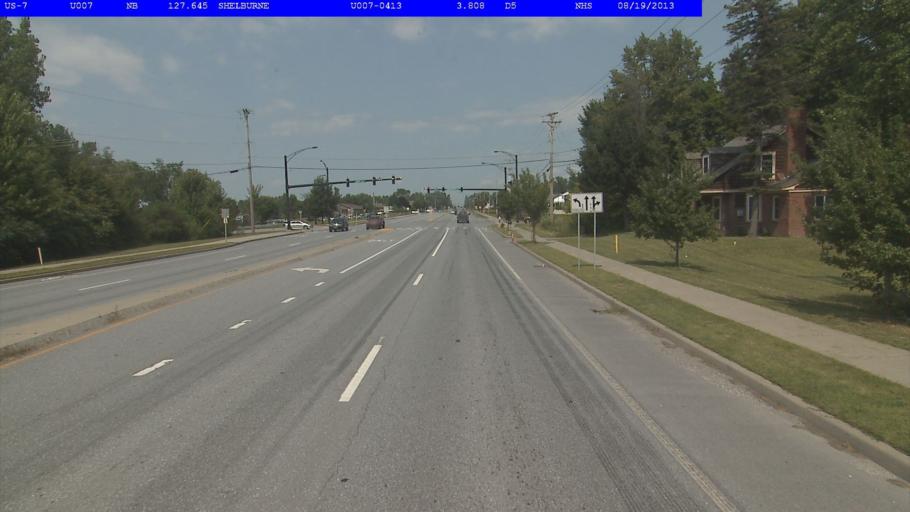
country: US
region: Vermont
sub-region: Chittenden County
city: Burlington
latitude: 44.4052
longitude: -73.2169
